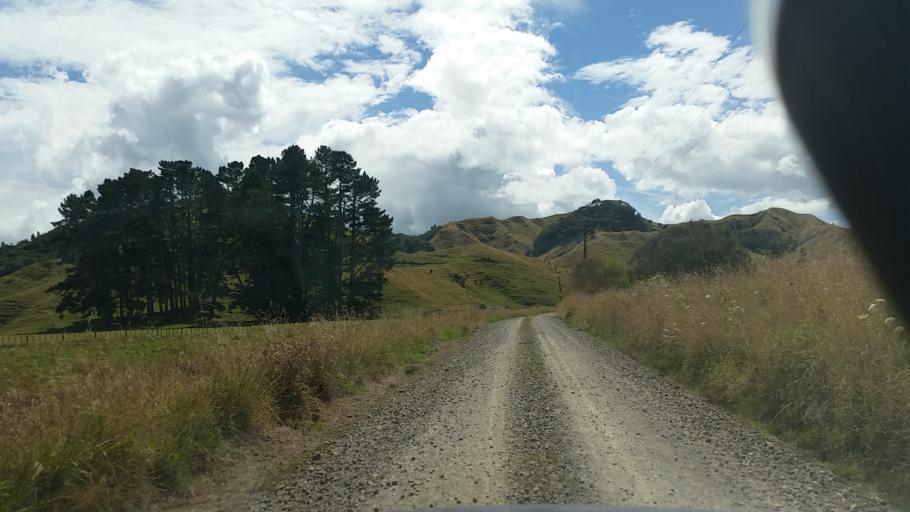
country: NZ
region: Taranaki
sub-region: South Taranaki District
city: Eltham
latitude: -39.2267
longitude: 174.5637
